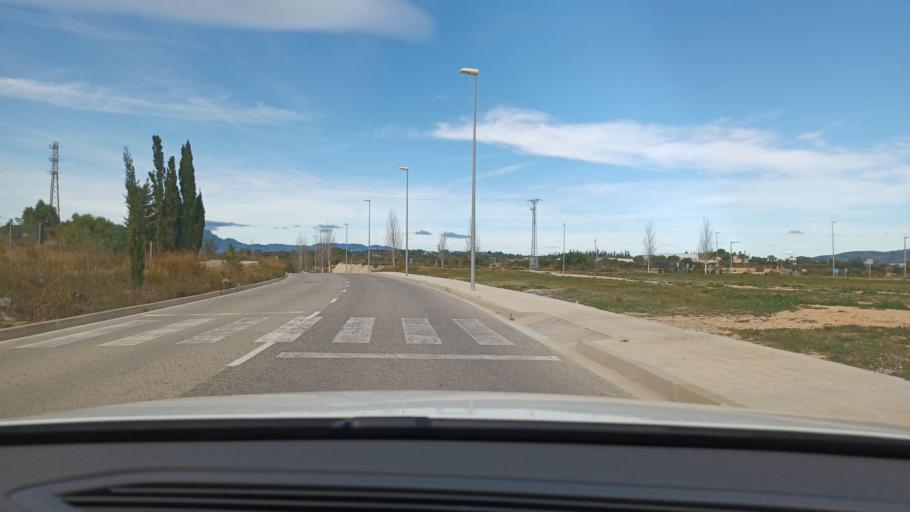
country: ES
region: Catalonia
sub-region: Provincia de Tarragona
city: Amposta
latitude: 40.7096
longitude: 0.5679
